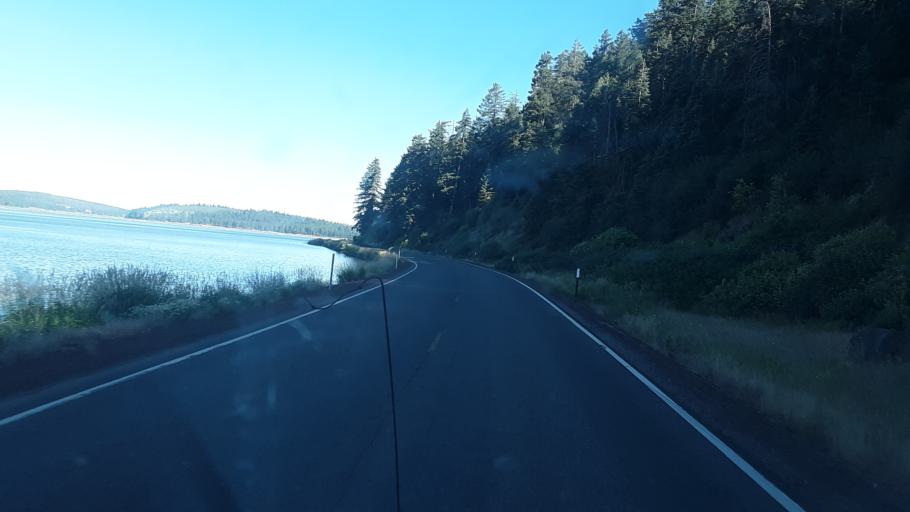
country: US
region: Oregon
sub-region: Klamath County
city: Klamath Falls
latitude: 42.3072
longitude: -121.9392
